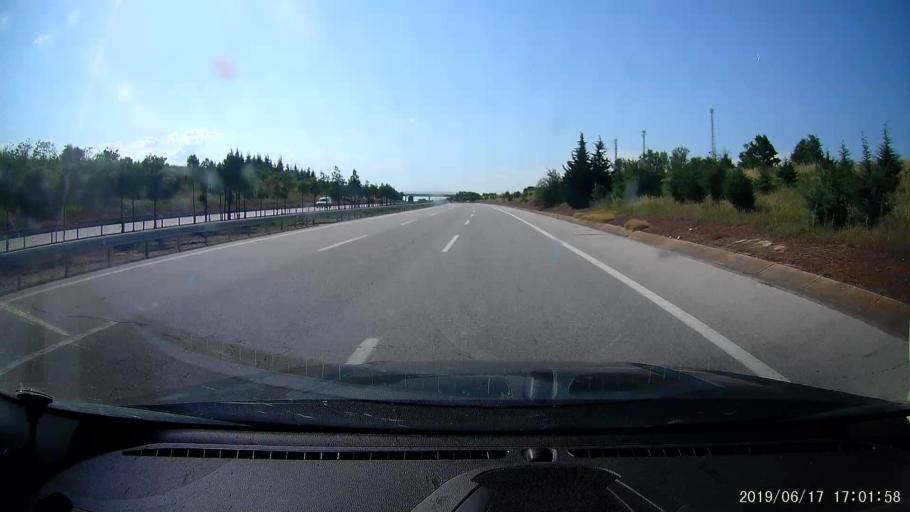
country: TR
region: Edirne
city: Haskoy
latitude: 41.6344
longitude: 26.7922
